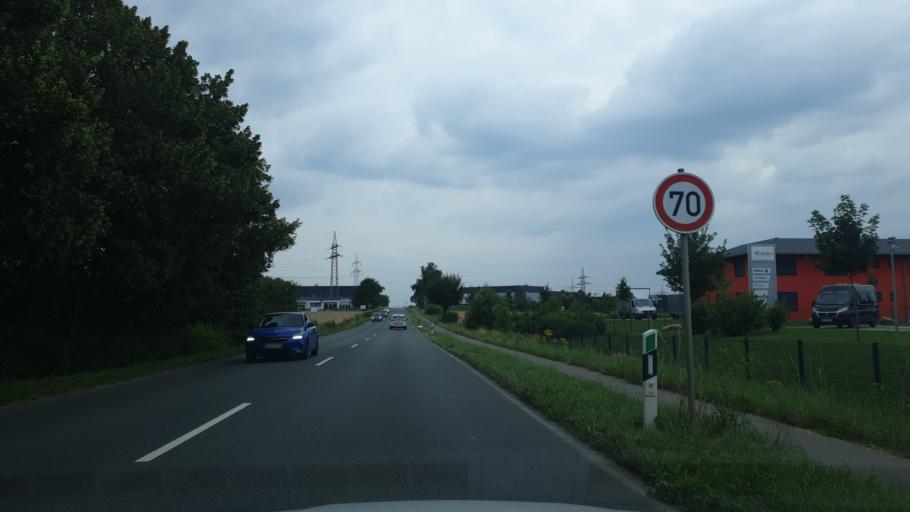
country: DE
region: North Rhine-Westphalia
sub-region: Regierungsbezirk Detmold
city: Lage
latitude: 51.9780
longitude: 8.8169
